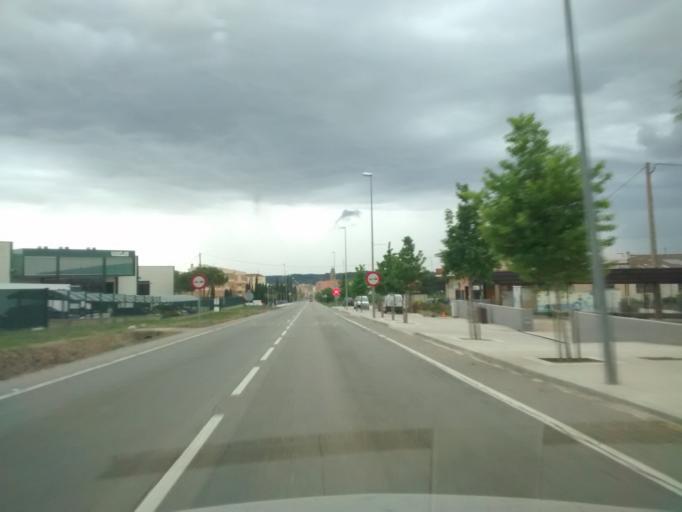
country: ES
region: Catalonia
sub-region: Provincia de Tarragona
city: Gandesa
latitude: 41.0487
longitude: 0.4465
